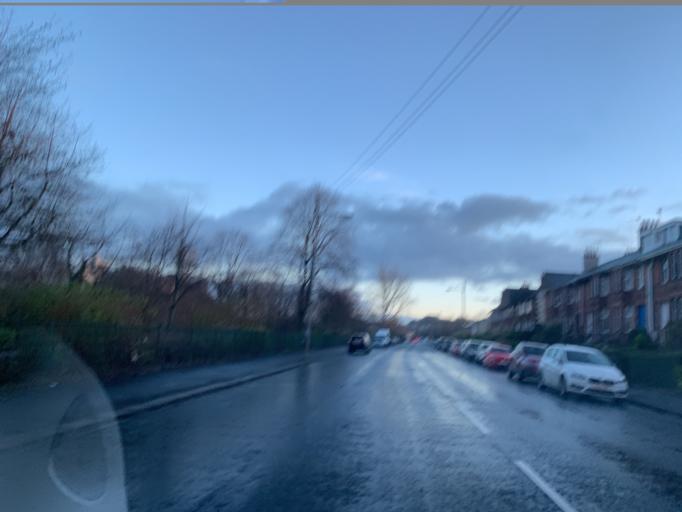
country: GB
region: Scotland
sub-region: East Renfrewshire
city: Giffnock
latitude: 55.8199
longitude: -4.2955
